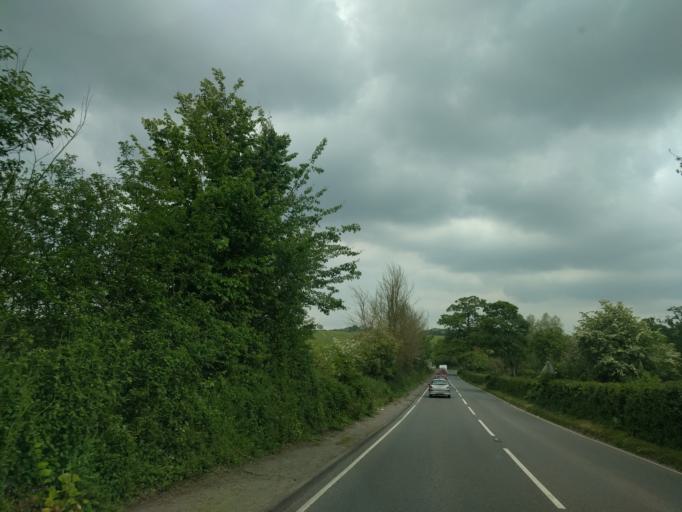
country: GB
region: England
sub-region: Somerset
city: Ilchester
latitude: 51.0561
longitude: -2.7212
